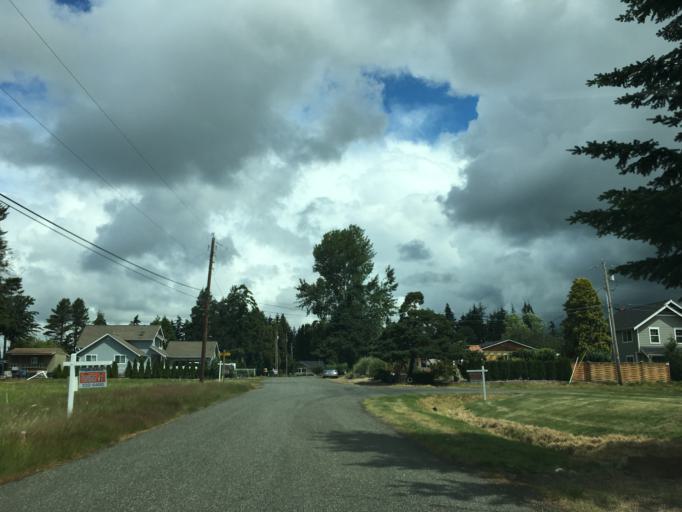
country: US
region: Washington
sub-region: Whatcom County
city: Blaine
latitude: 48.9693
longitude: -122.7330
